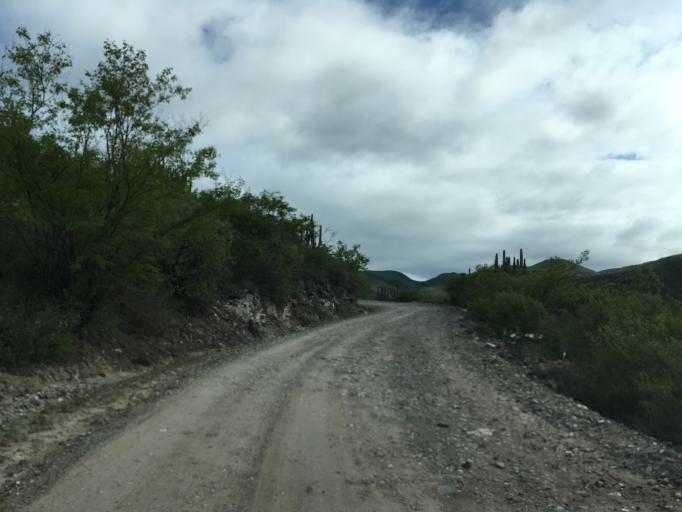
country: MX
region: Hidalgo
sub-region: Metztitlan
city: Fontezuelas
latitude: 20.6428
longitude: -98.9386
